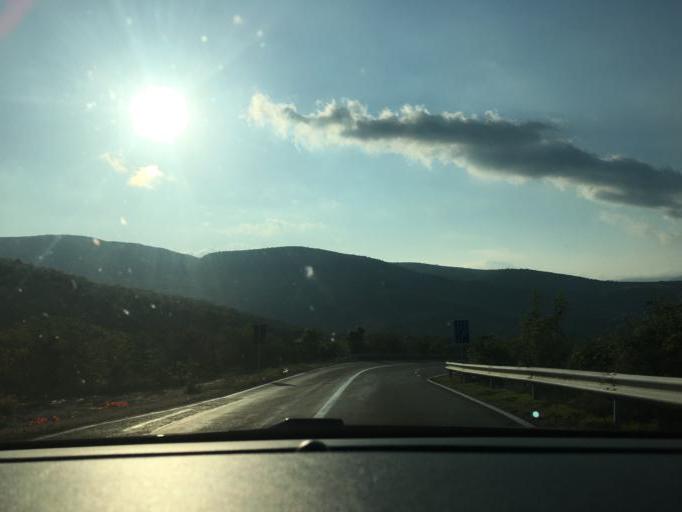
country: MK
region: Valandovo
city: Valandovo
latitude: 41.3240
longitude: 22.5965
